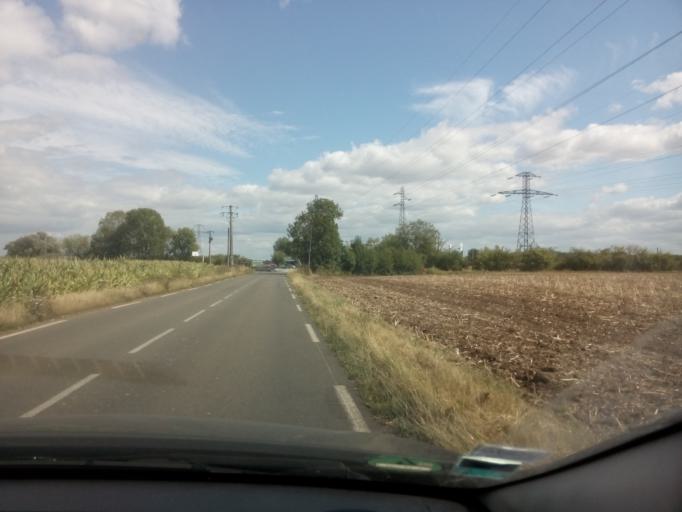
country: FR
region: Ile-de-France
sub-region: Departement de l'Essonne
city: Vauhallan
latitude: 48.7446
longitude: 2.1873
